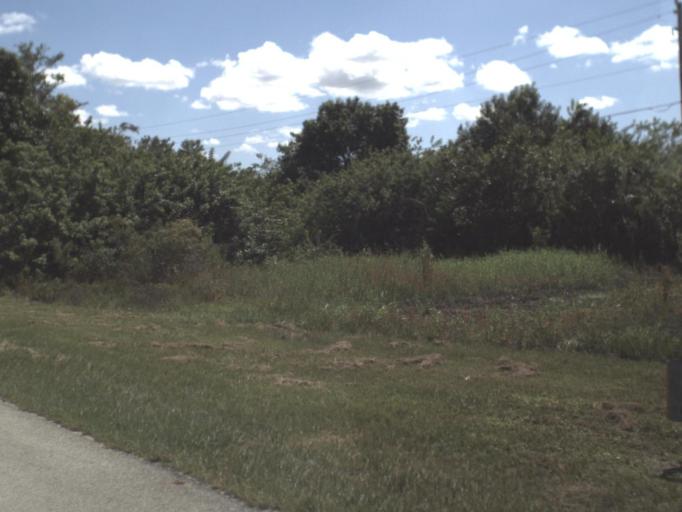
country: US
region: Florida
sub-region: Collier County
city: Lely Resort
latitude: 26.0254
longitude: -81.6399
